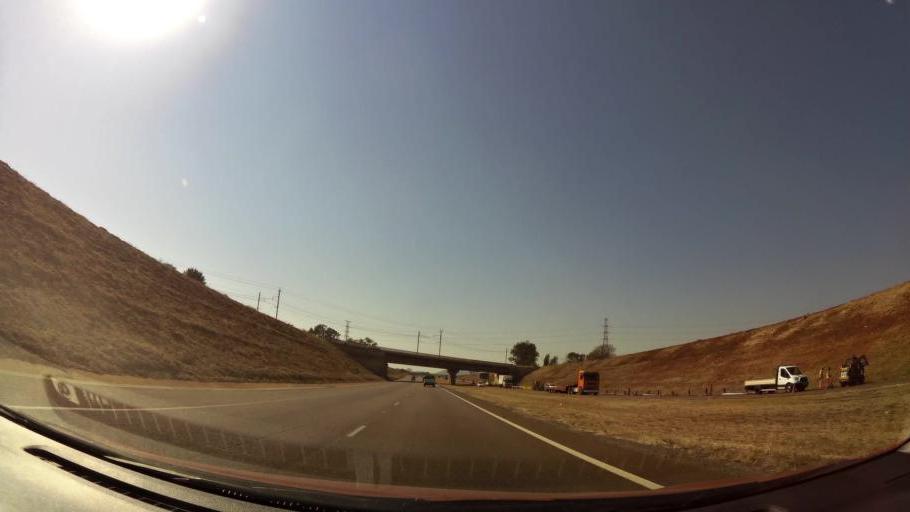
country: ZA
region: Gauteng
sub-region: City of Tshwane Metropolitan Municipality
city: Pretoria
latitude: -25.6504
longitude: 28.1389
